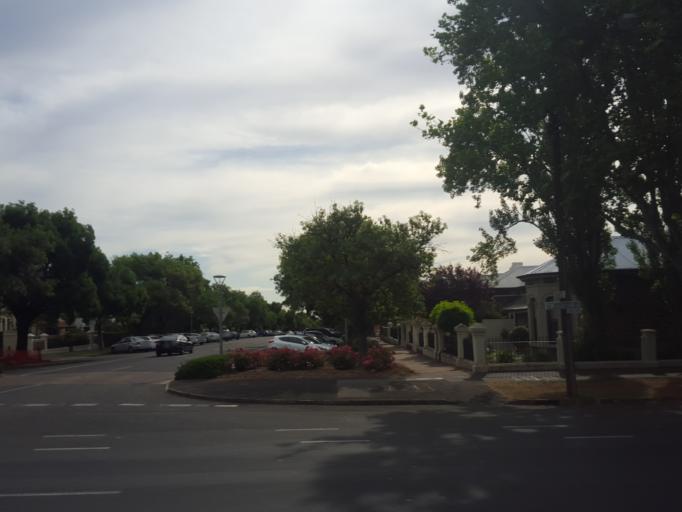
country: AU
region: South Australia
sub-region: Adelaide
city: North Adelaide
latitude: -34.9041
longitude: 138.5904
